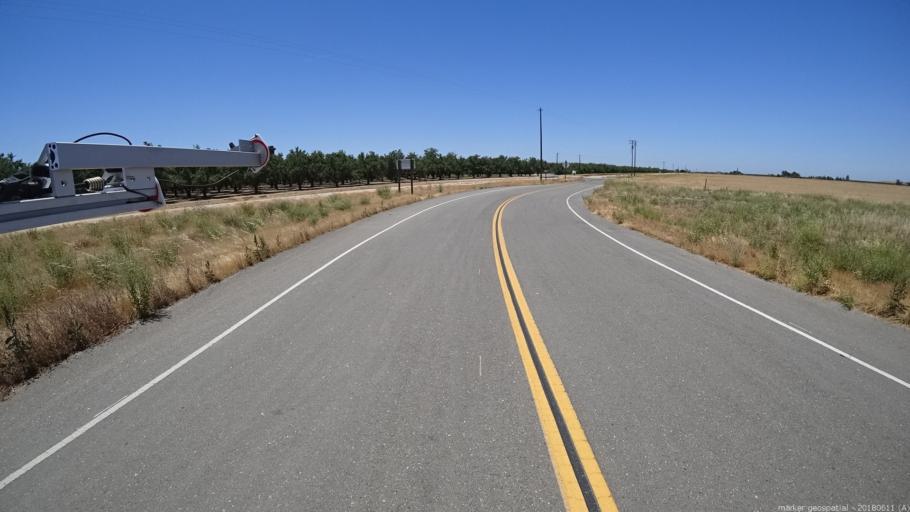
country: US
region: California
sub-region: Madera County
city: Fairmead
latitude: 37.0547
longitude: -120.1736
